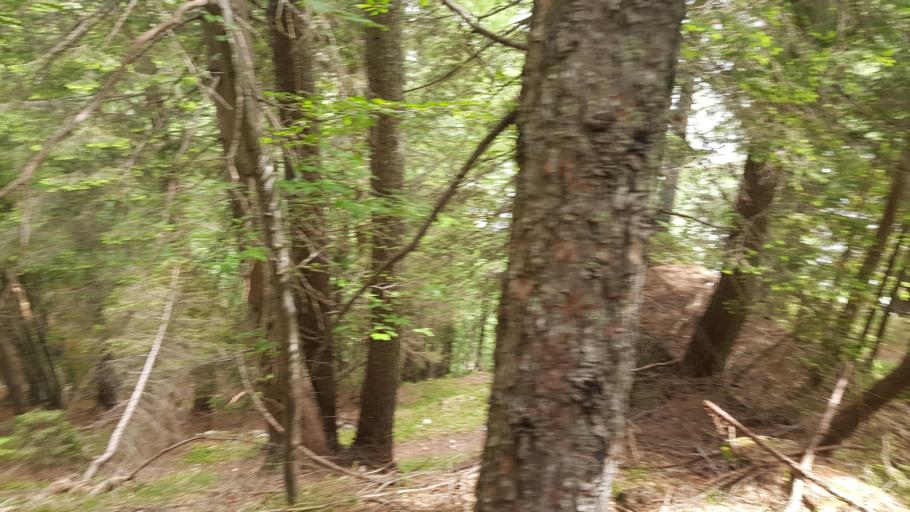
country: IT
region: Friuli Venezia Giulia
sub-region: Provincia di Udine
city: Pontebba
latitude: 46.5350
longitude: 13.2866
